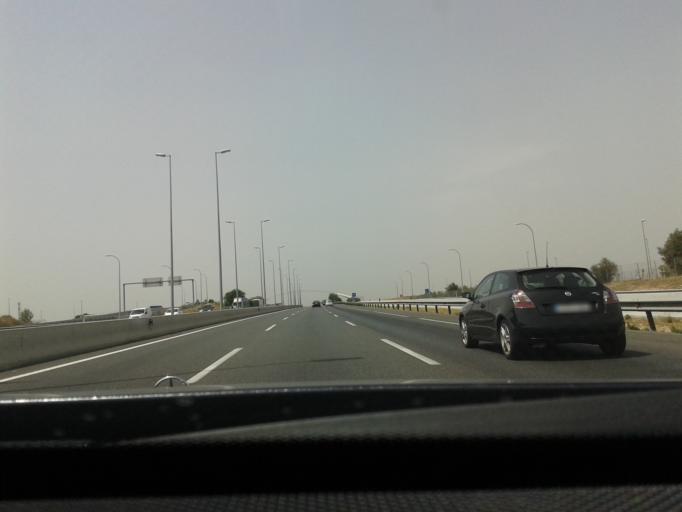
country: ES
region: Madrid
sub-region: Provincia de Madrid
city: Torrejon de Ardoz
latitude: 40.4694
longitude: -3.4318
